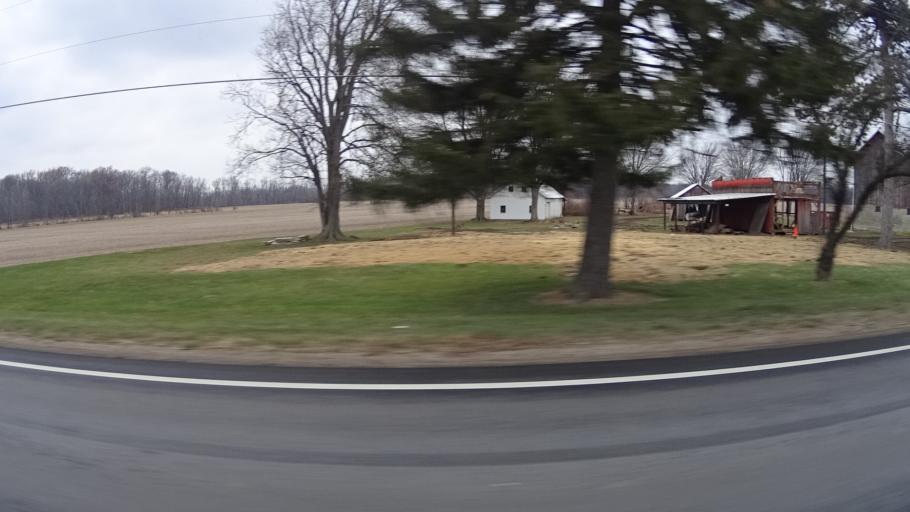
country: US
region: Ohio
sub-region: Lorain County
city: Amherst
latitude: 41.3692
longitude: -82.1783
